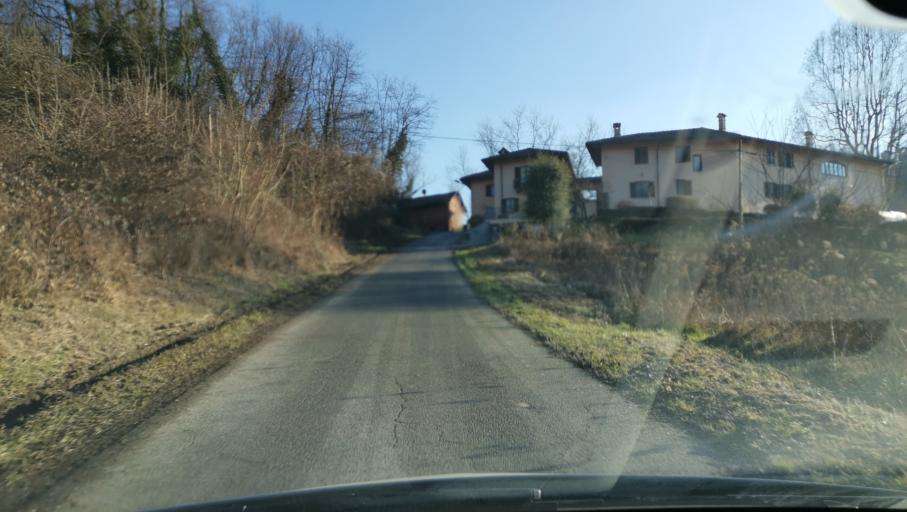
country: IT
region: Piedmont
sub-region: Provincia di Torino
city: San Raffaele Cimena
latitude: 45.1380
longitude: 7.8614
